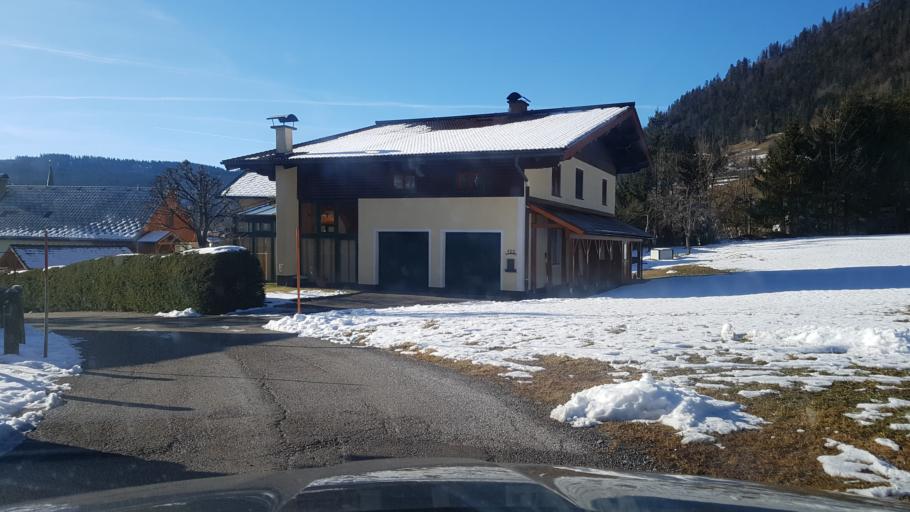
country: AT
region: Salzburg
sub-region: Politischer Bezirk Salzburg-Umgebung
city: Strobl
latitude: 47.5949
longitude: 13.4676
